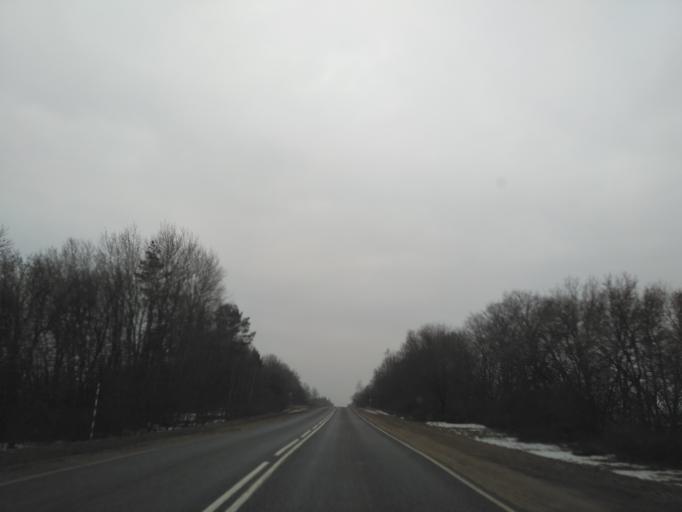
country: BY
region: Minsk
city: Snow
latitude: 53.3174
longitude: 26.4312
